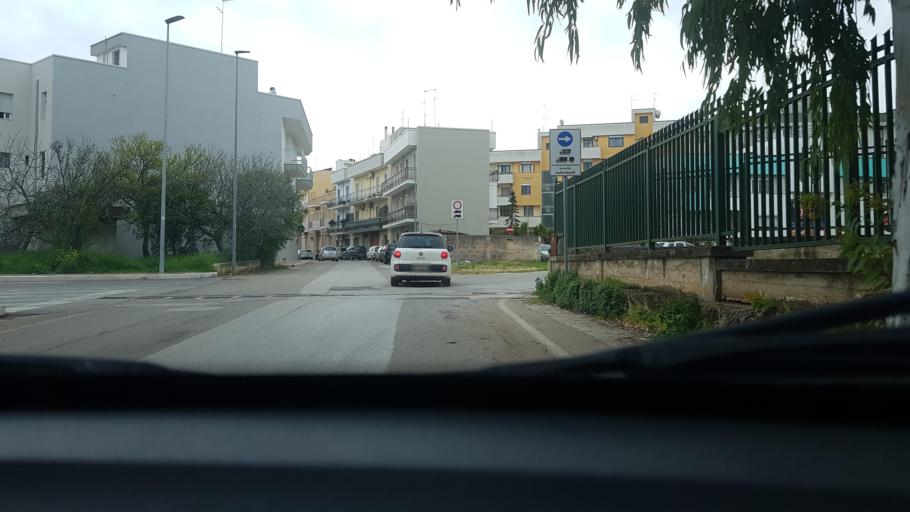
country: IT
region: Apulia
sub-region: Provincia di Bari
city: Noicattaro
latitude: 41.0363
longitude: 16.9833
